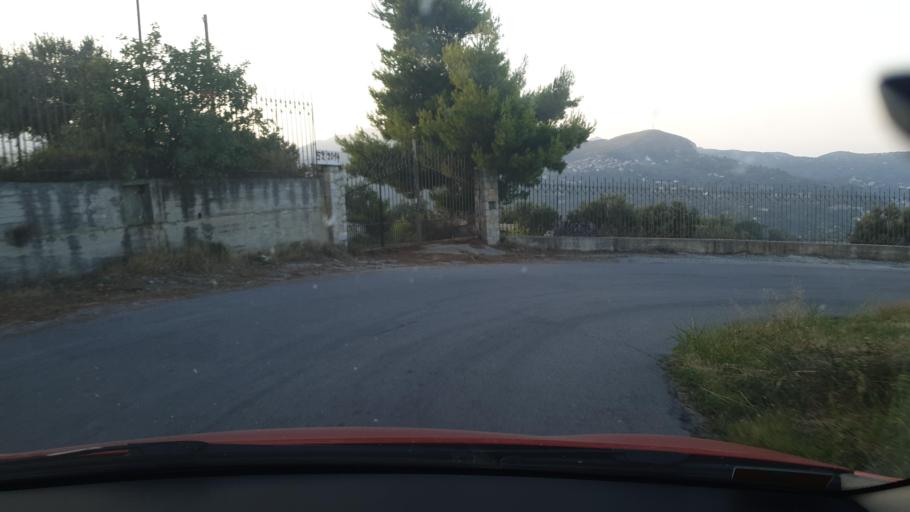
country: GR
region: Central Greece
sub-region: Nomos Evvoias
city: Oxilithos
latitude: 38.5934
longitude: 24.1191
